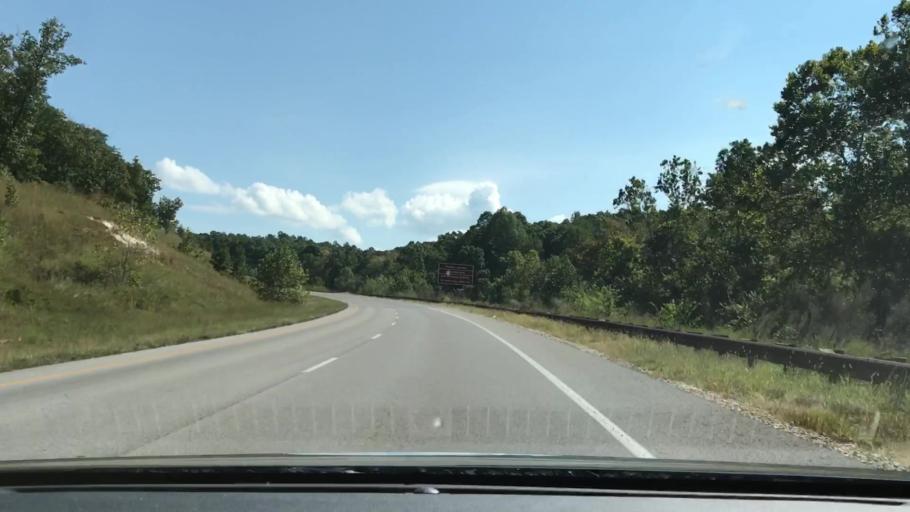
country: US
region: Kentucky
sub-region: Trigg County
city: Cadiz
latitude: 36.7775
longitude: -88.0871
